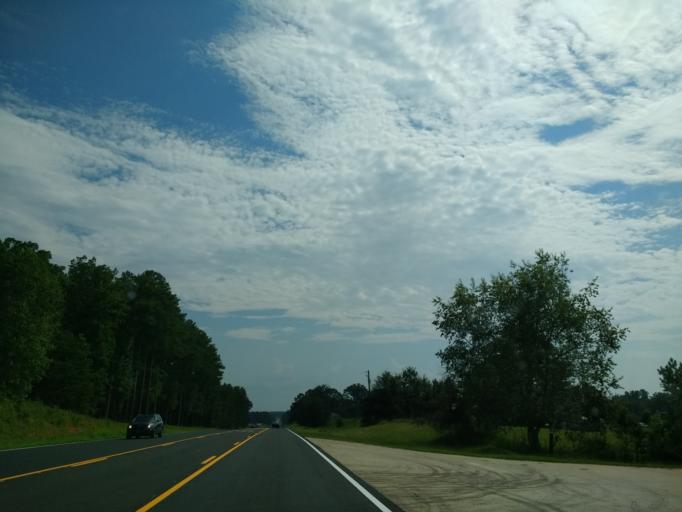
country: US
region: Georgia
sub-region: White County
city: Cleveland
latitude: 34.4893
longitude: -83.7588
